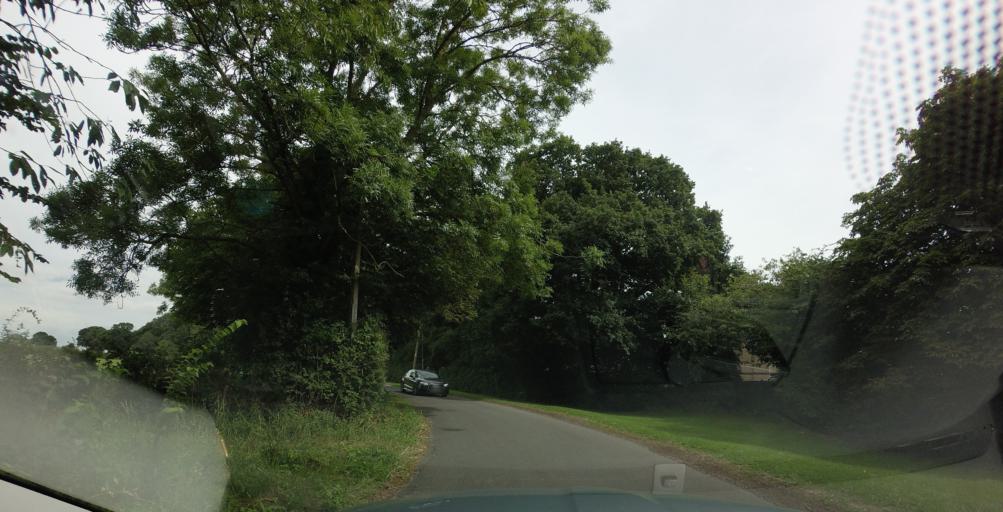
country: GB
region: England
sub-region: North Yorkshire
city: Ripon
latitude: 54.1377
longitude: -1.4769
